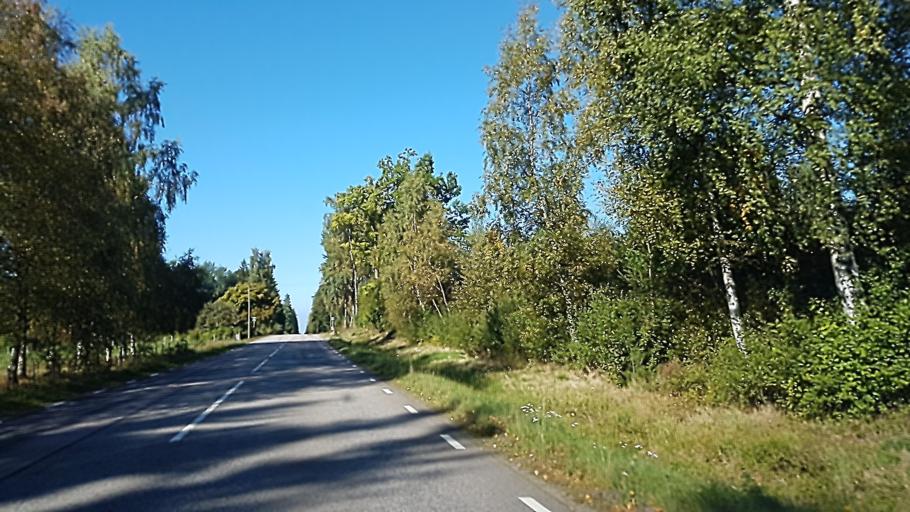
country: SE
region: Kronoberg
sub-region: Ljungby Kommun
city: Ljungby
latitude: 56.8263
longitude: 14.0275
